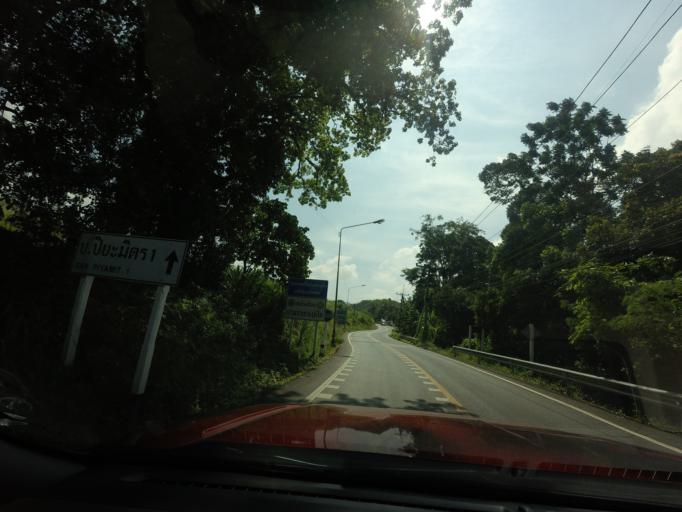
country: TH
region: Yala
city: Betong
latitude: 5.8059
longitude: 101.0726
